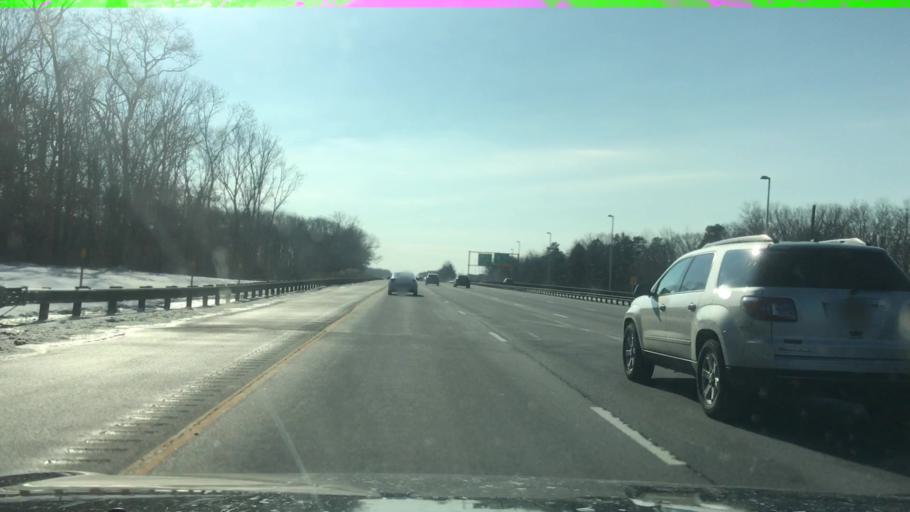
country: US
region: New Jersey
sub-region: Monmouth County
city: Shark River Hills
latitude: 40.1691
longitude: -74.1012
